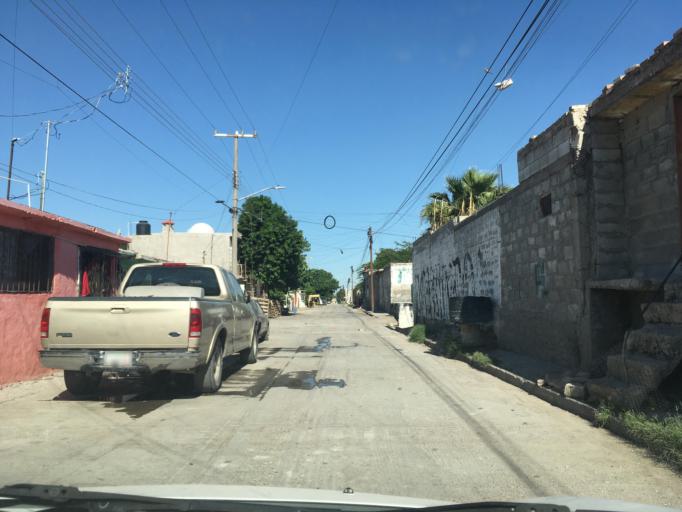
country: MX
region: Durango
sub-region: Lerdo
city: El Huarache (El Guarache)
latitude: 25.5428
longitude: -103.4749
